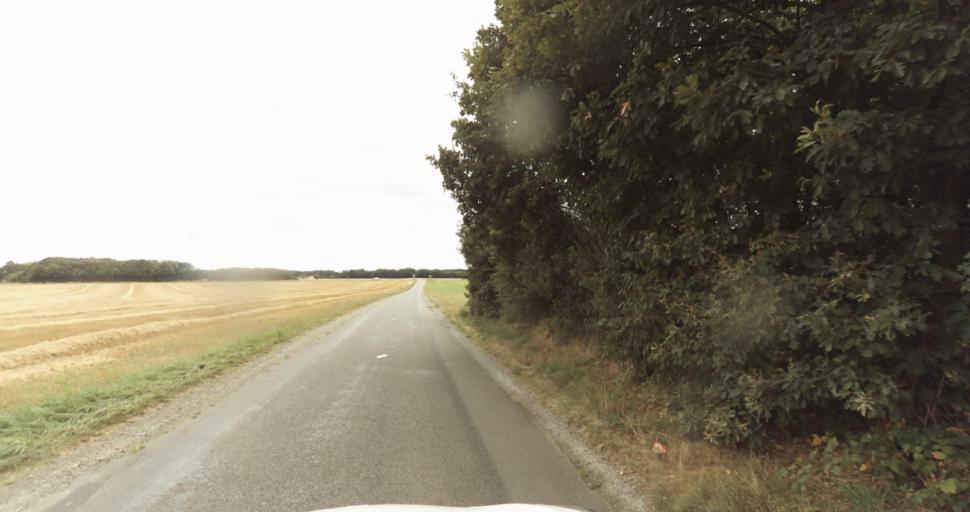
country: FR
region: Haute-Normandie
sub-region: Departement de l'Eure
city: Saint-Germain-sur-Avre
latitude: 48.8086
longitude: 1.2690
